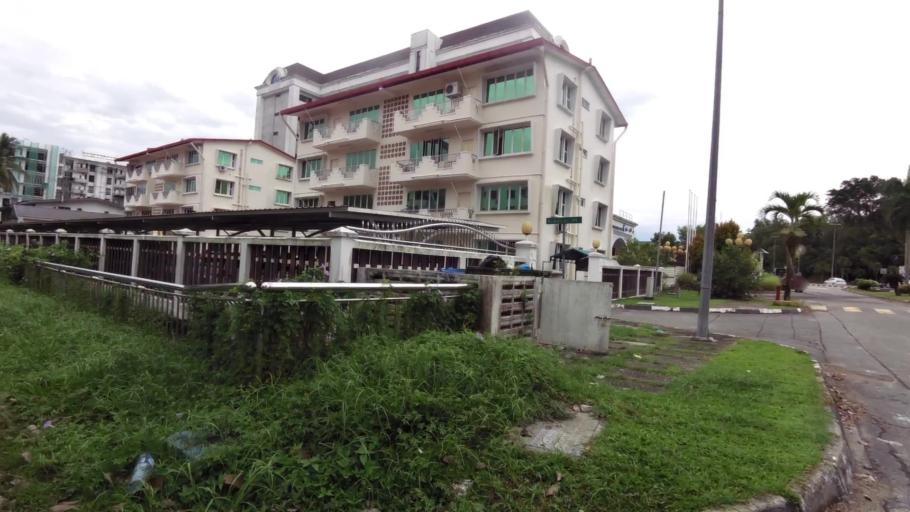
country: BN
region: Brunei and Muara
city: Bandar Seri Begawan
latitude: 4.9057
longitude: 114.9305
